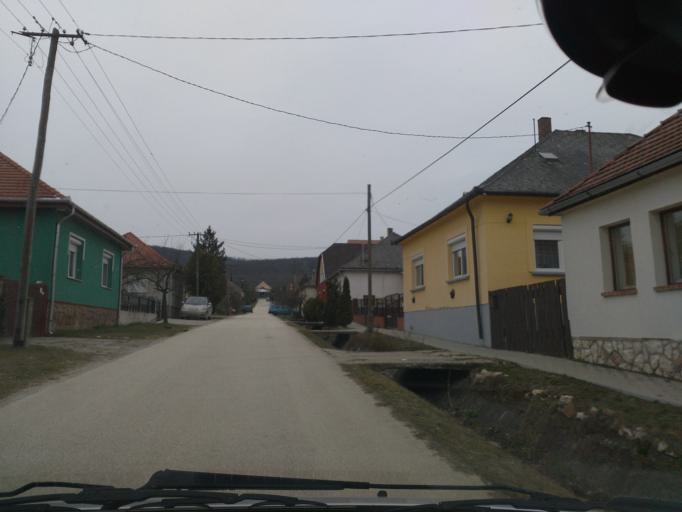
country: HU
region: Komarom-Esztergom
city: Piliscsev
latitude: 47.6707
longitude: 18.8138
